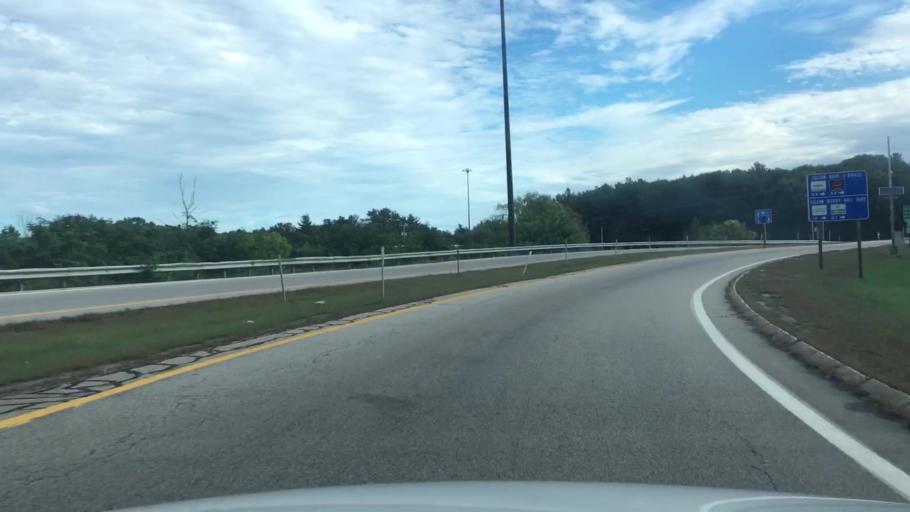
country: US
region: Maine
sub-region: York County
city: Kittery
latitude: 43.1051
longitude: -70.7500
